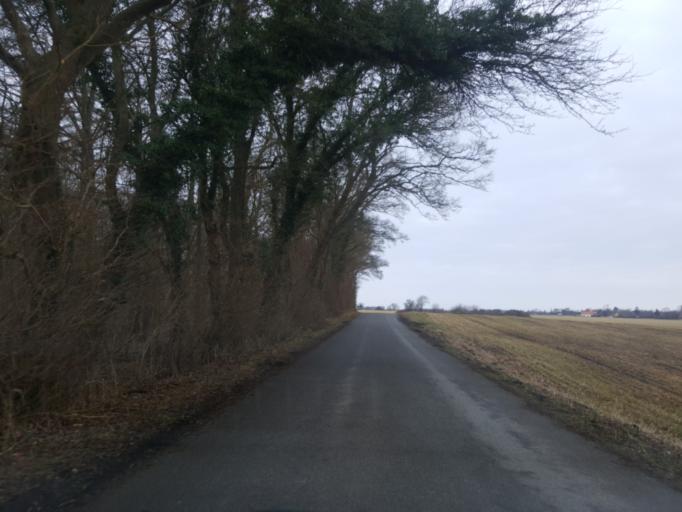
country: DK
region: Zealand
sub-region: Vordingborg Kommune
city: Neder Vindinge
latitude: 55.0340
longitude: 11.8448
